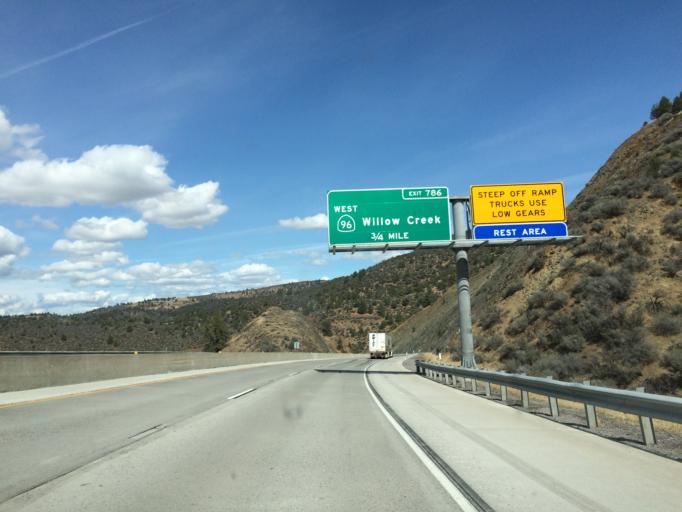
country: US
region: California
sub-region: Siskiyou County
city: Yreka
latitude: 41.8435
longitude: -122.5740
